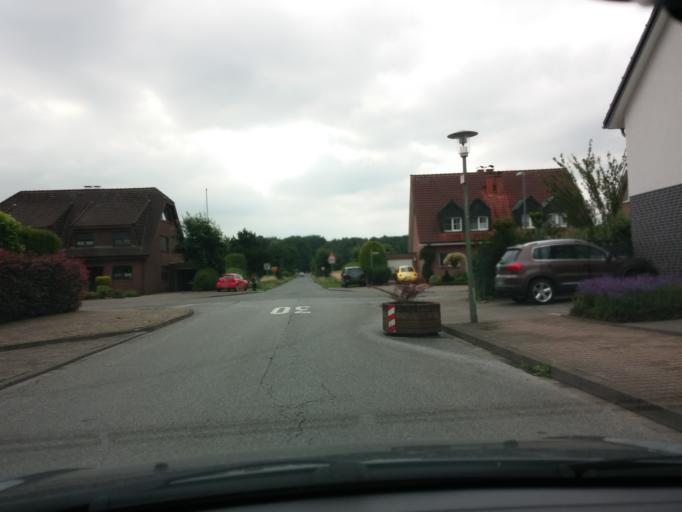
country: DE
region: North Rhine-Westphalia
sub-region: Regierungsbezirk Munster
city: Gladbeck
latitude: 51.6098
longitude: 6.9694
